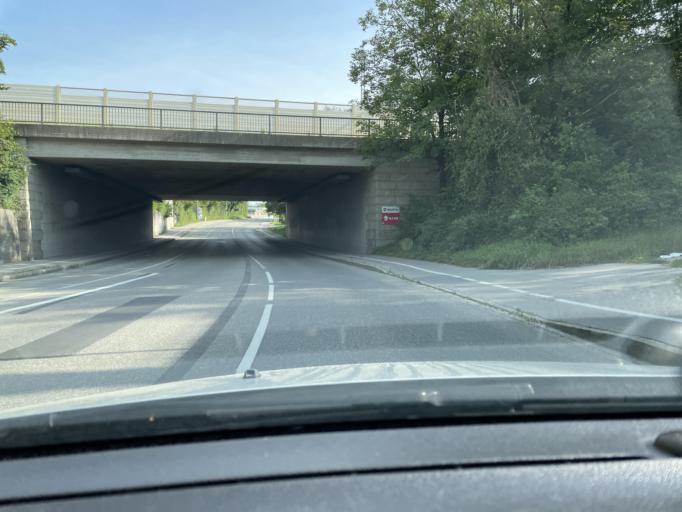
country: DE
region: Bavaria
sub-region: Upper Bavaria
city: Muehldorf
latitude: 48.2478
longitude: 12.5239
